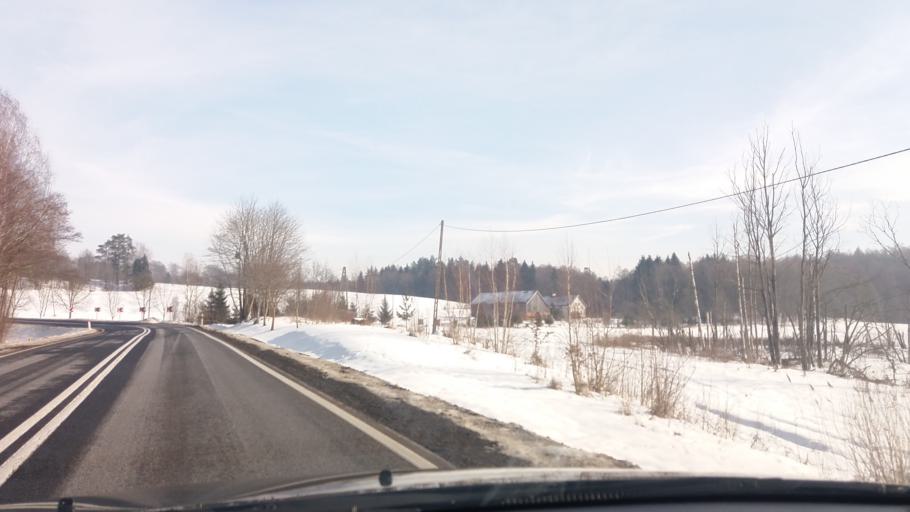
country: PL
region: Warmian-Masurian Voivodeship
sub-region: Powiat olsztynski
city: Czerwonka
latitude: 53.9454
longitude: 20.9013
